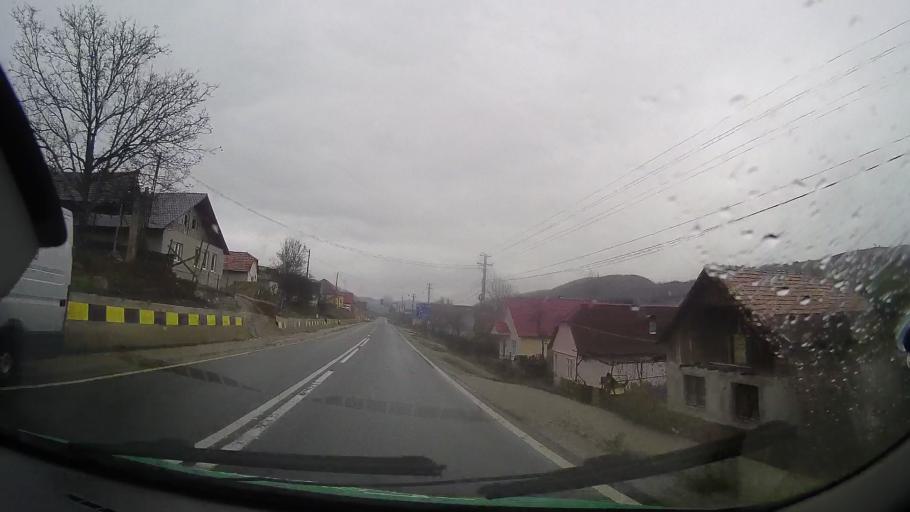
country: RO
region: Bistrita-Nasaud
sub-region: Comuna Galatii Bistritei
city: Galatii Bistritei
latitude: 46.9498
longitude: 24.4514
